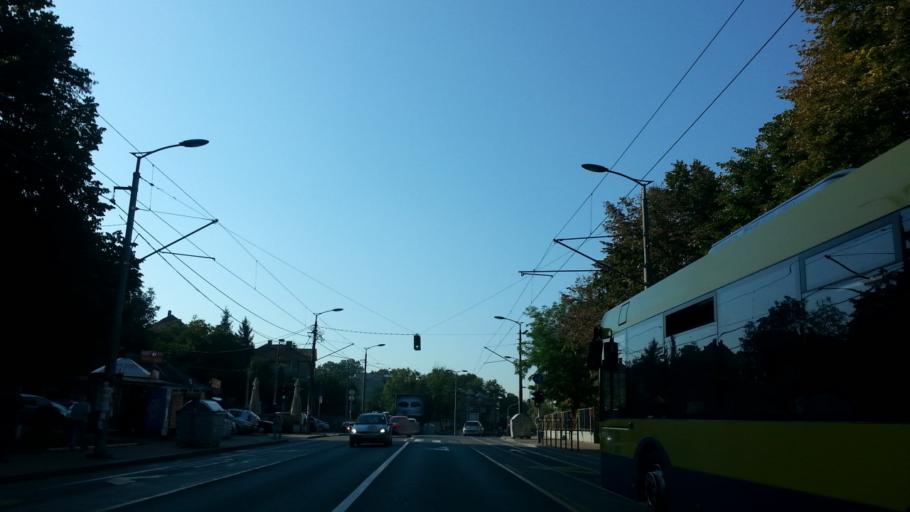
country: RS
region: Central Serbia
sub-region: Belgrade
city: Cukarica
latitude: 44.7714
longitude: 20.4142
